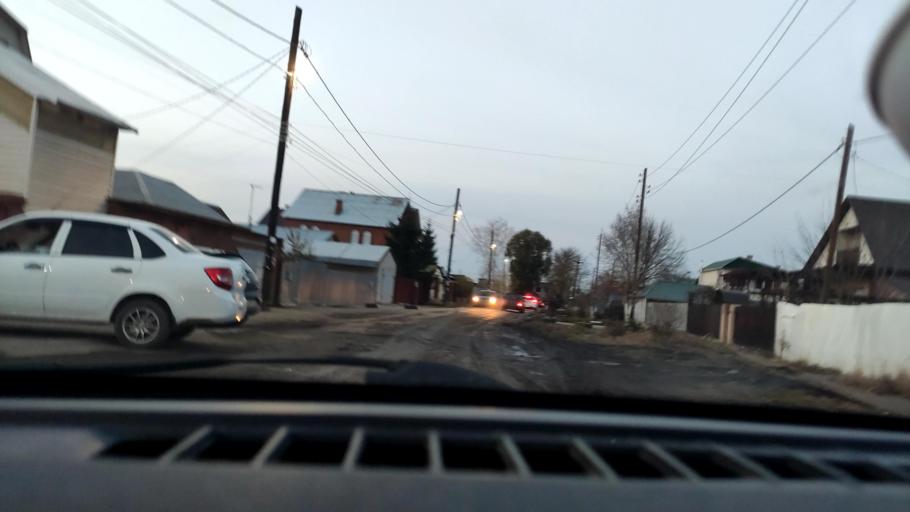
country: RU
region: Samara
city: Samara
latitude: 53.1334
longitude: 50.0948
